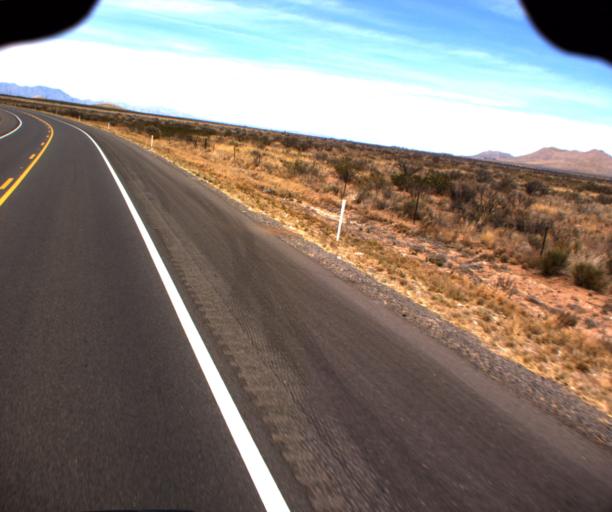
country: US
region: Arizona
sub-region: Cochise County
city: Willcox
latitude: 31.9046
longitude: -109.7180
